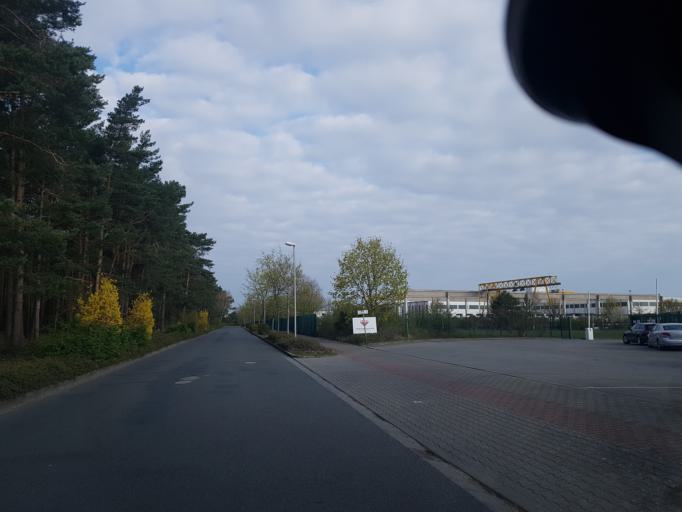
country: DE
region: Brandenburg
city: Linthe
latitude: 52.1644
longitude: 12.7792
